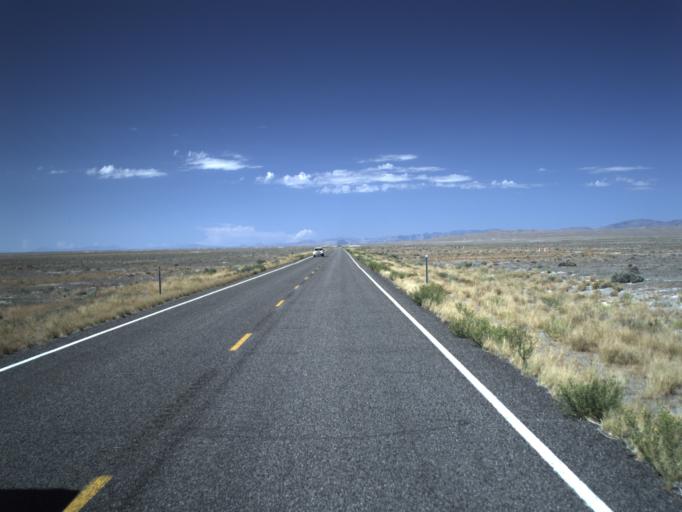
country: US
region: Utah
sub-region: Millard County
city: Delta
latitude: 39.2223
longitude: -112.9456
